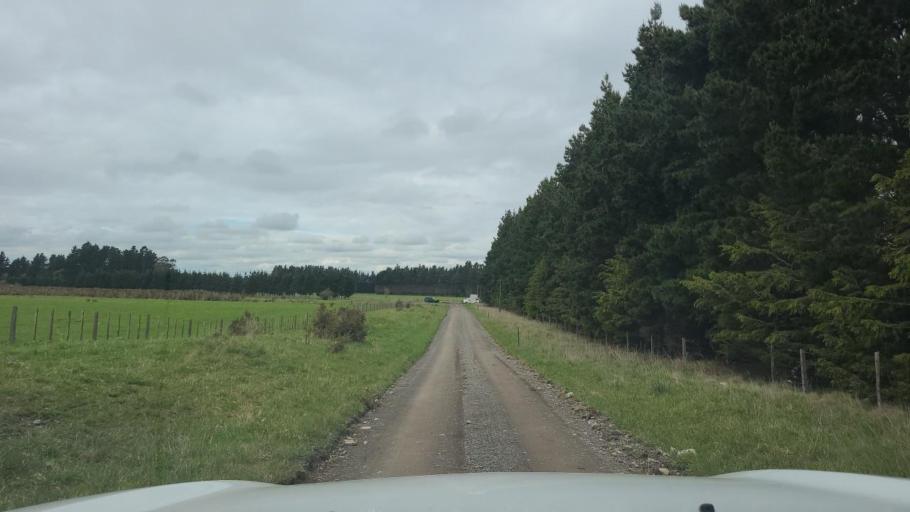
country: NZ
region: Wellington
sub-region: Upper Hutt City
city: Upper Hutt
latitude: -41.0913
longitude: 175.3536
